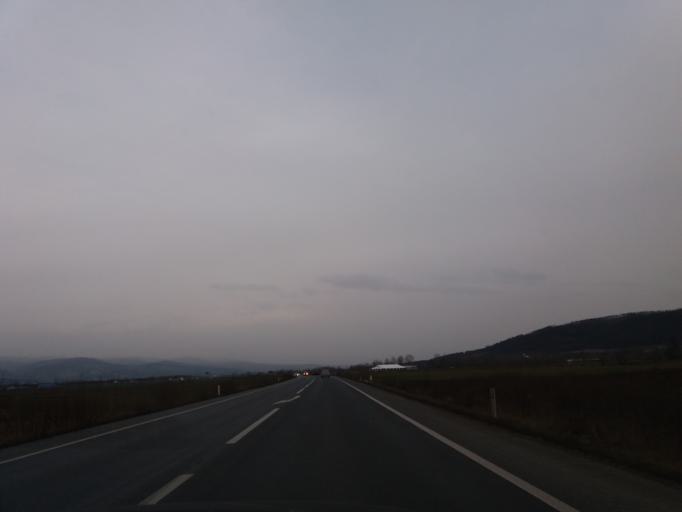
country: RO
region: Hunedoara
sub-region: Oras Simeria
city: Simeria
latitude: 45.8268
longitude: 23.0311
